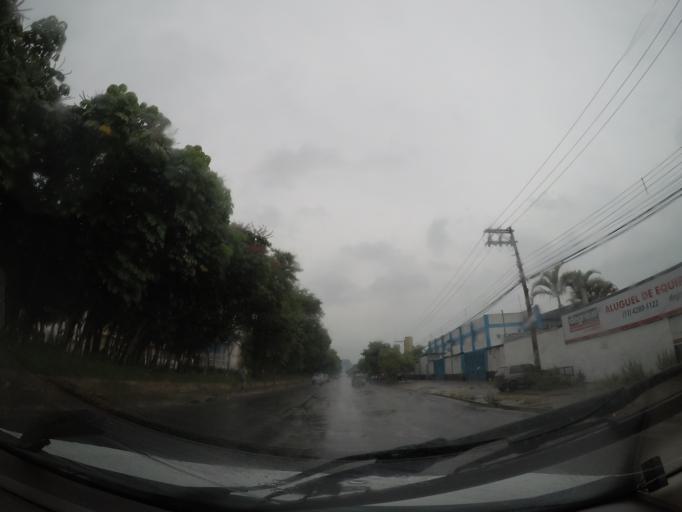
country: BR
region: Sao Paulo
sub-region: Guarulhos
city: Guarulhos
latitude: -23.4746
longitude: -46.4675
